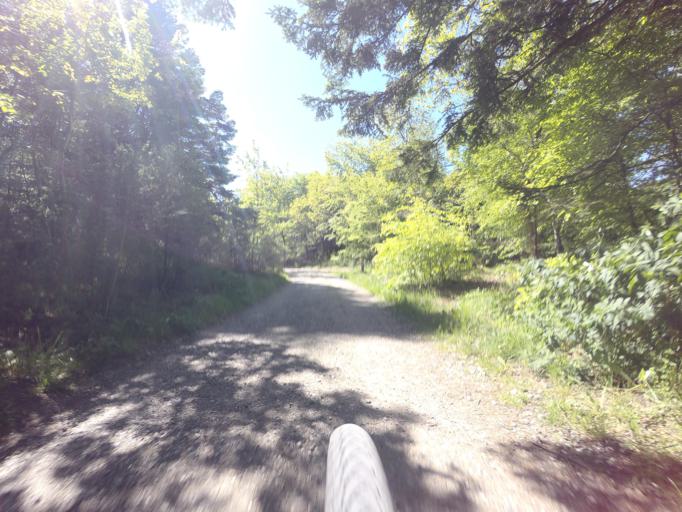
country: DK
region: North Denmark
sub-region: Jammerbugt Kommune
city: Pandrup
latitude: 57.2470
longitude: 9.6002
